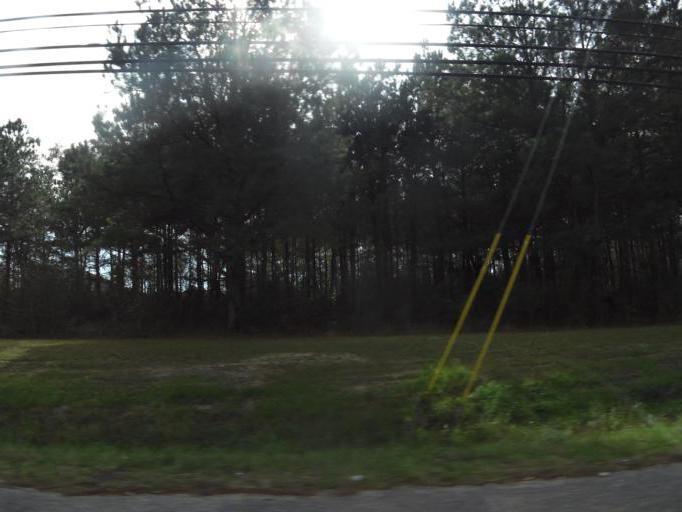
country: US
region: Alabama
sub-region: Houston County
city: Cowarts
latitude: 31.2012
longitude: -85.3421
